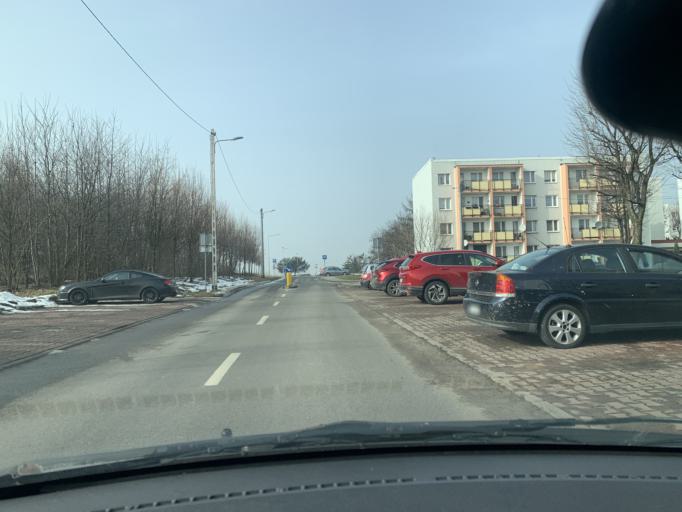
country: PL
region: Silesian Voivodeship
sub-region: Powiat tarnogorski
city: Radzionkow
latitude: 50.4045
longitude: 18.8959
